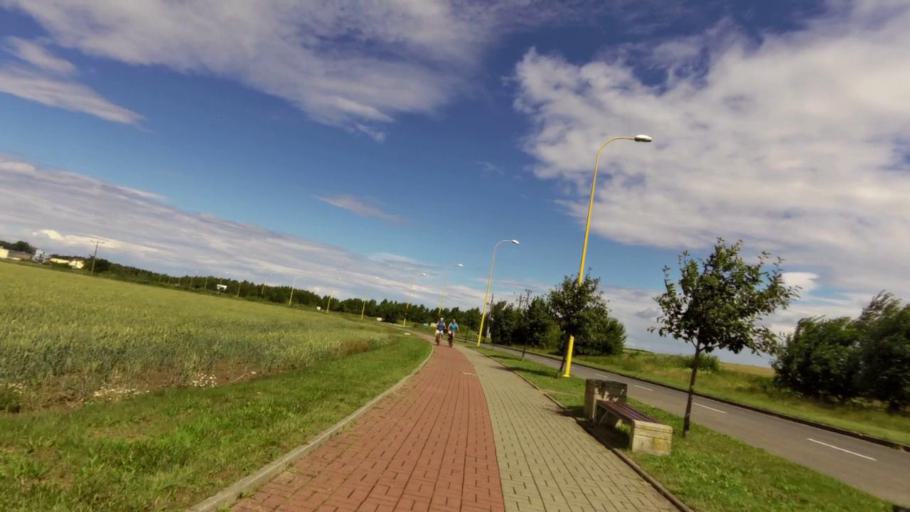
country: PL
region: West Pomeranian Voivodeship
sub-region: Powiat slawienski
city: Darlowo
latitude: 54.4416
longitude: 16.4063
